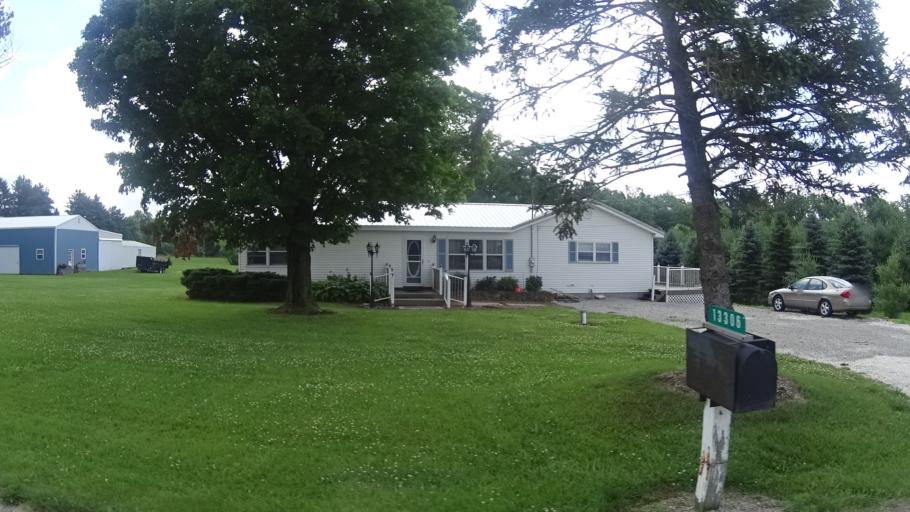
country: US
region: Ohio
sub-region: Huron County
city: Wakeman
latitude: 41.2986
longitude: -82.3875
